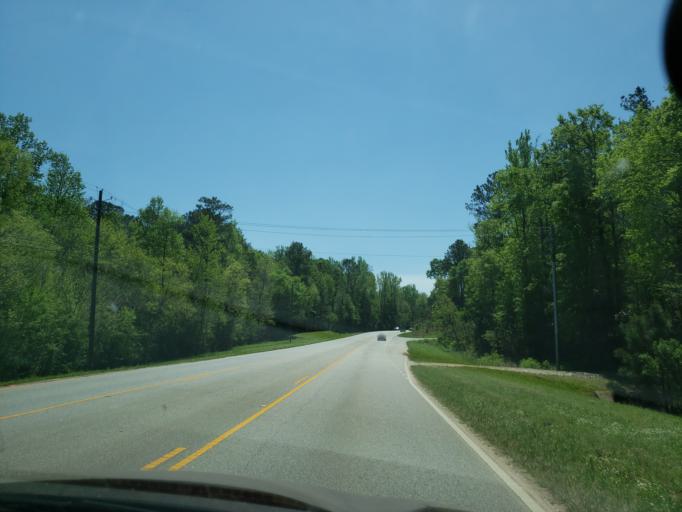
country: US
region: Alabama
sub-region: Lee County
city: Auburn
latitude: 32.6415
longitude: -85.5039
